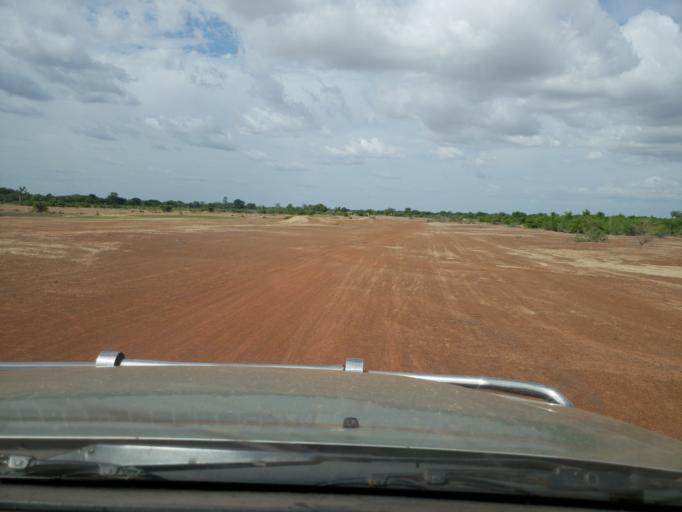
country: ML
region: Segou
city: Bla
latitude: 12.7048
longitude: -5.7241
